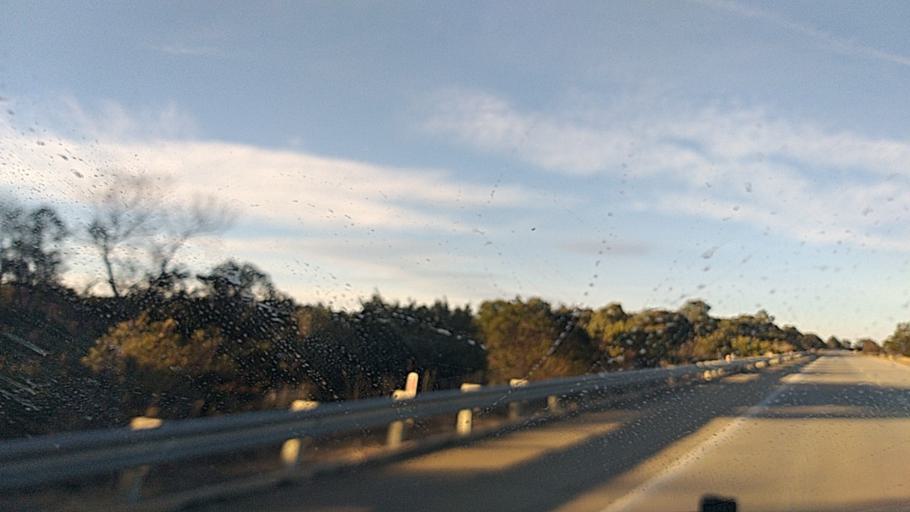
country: AU
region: New South Wales
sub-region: Yass Valley
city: Gundaroo
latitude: -35.1276
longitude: 149.3425
